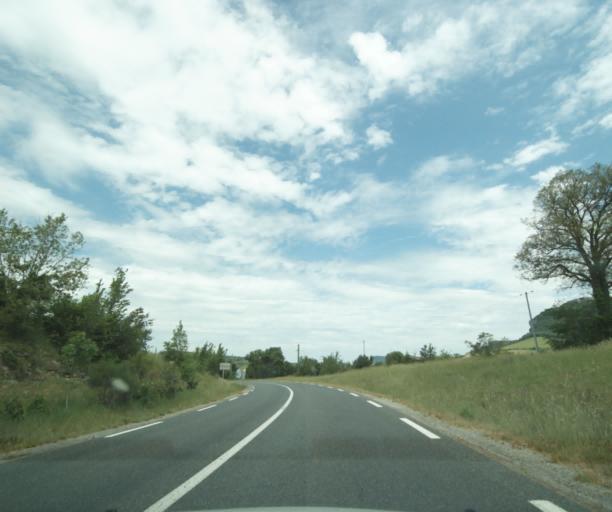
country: FR
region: Midi-Pyrenees
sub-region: Departement de l'Aveyron
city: Saint-Affrique
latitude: 43.9644
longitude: 2.9648
